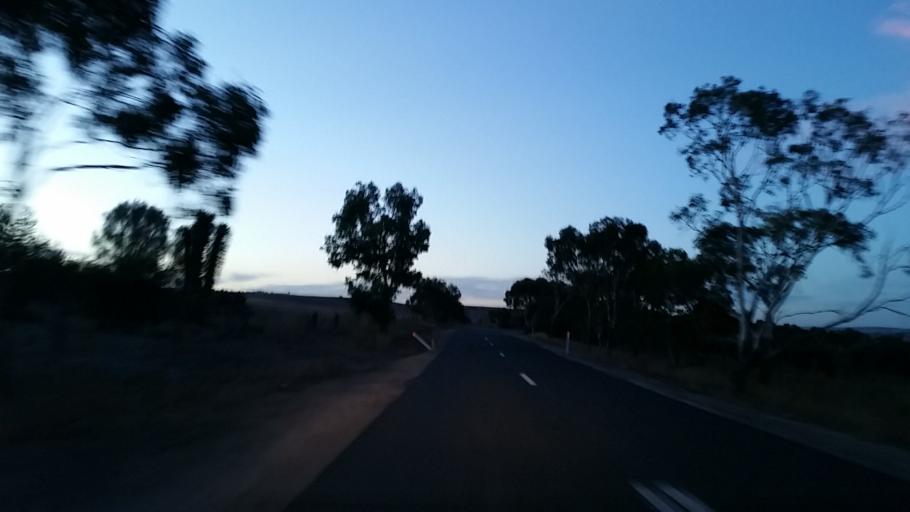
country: AU
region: South Australia
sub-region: Mount Barker
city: Callington
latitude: -35.1101
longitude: 139.0379
